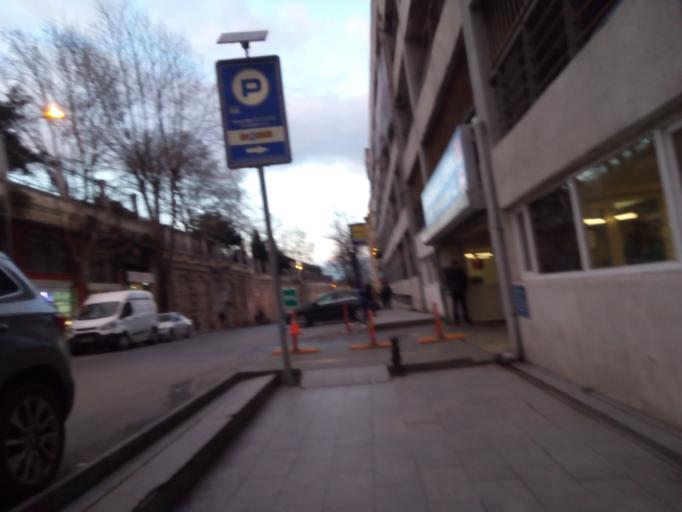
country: TR
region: Istanbul
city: Eminoenue
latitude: 41.0133
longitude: 28.9658
